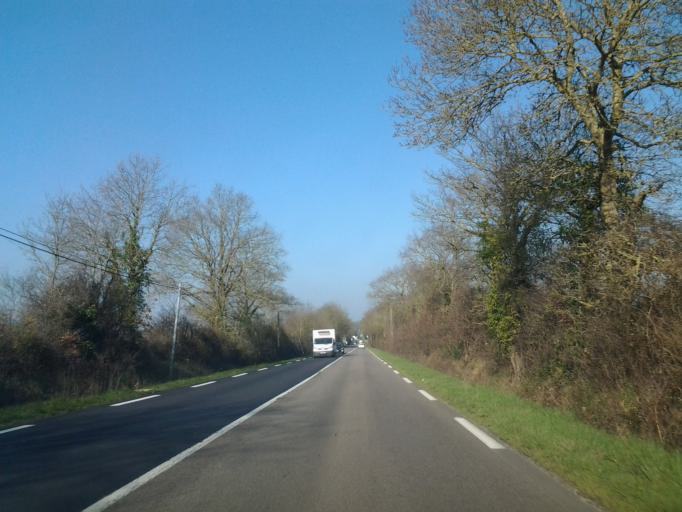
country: FR
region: Pays de la Loire
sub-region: Departement de la Vendee
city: Saint-Christophe-du-Ligneron
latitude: 46.8128
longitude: -1.7498
